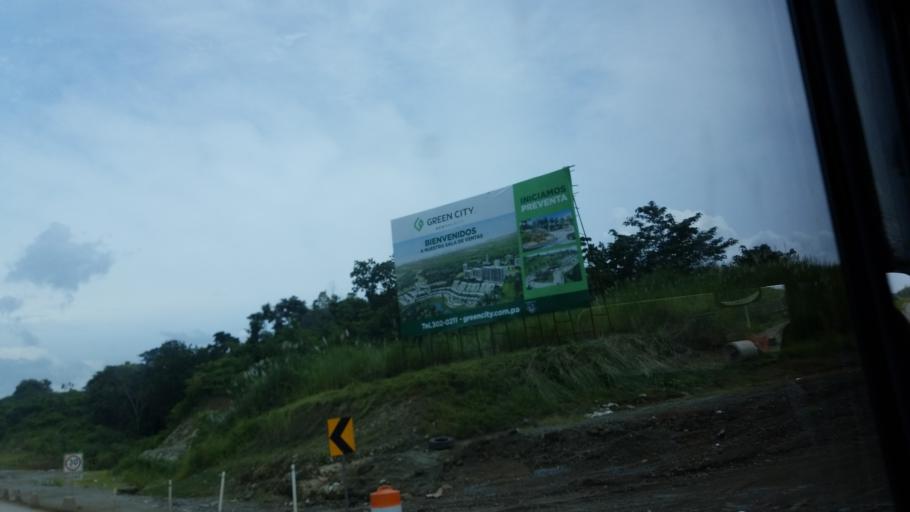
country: PA
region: Panama
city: San Miguelito
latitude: 9.0984
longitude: -79.4743
